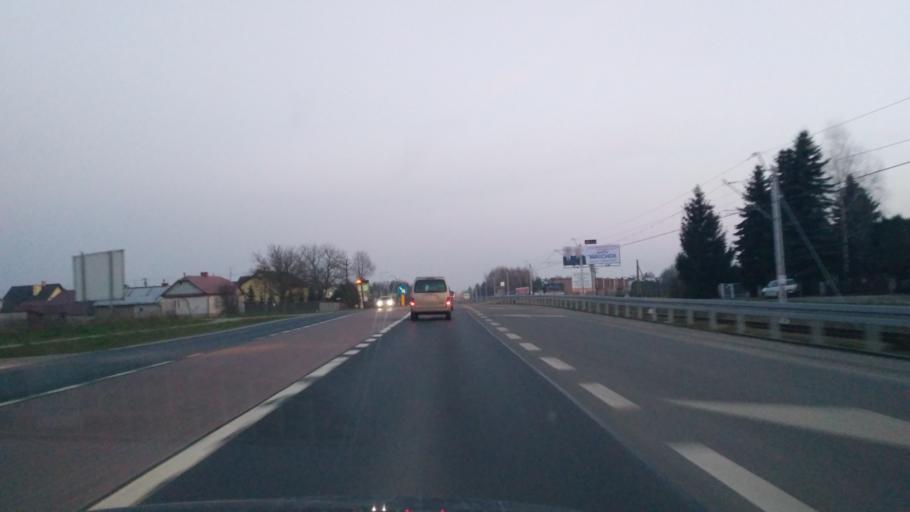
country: PL
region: Subcarpathian Voivodeship
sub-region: Powiat rzeszowski
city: Rudna Mala
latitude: 50.0818
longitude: 21.9851
